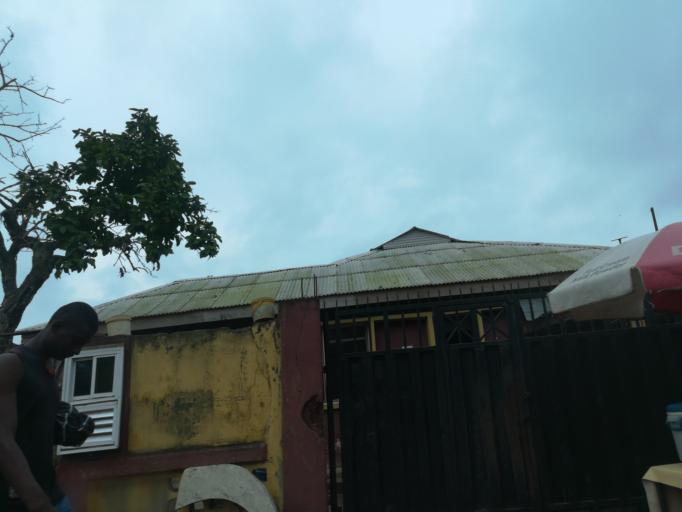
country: NG
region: Lagos
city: Oshodi
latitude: 6.5683
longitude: 3.3453
